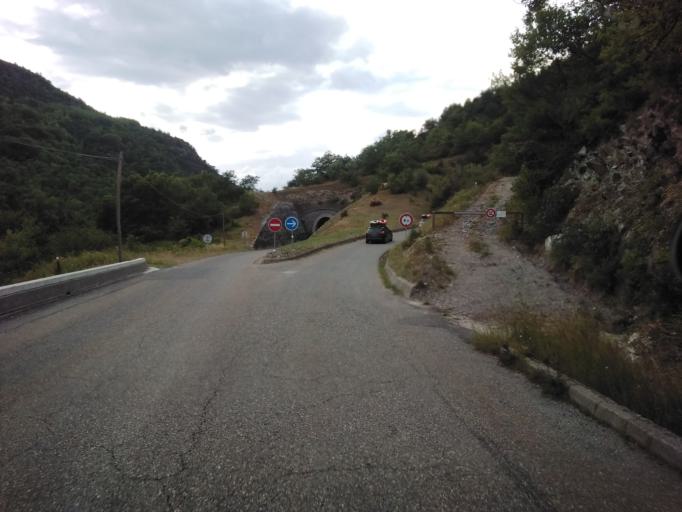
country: FR
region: Provence-Alpes-Cote d'Azur
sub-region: Departement des Alpes-de-Haute-Provence
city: Seyne-les-Alpes
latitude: 44.4574
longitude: 6.3824
